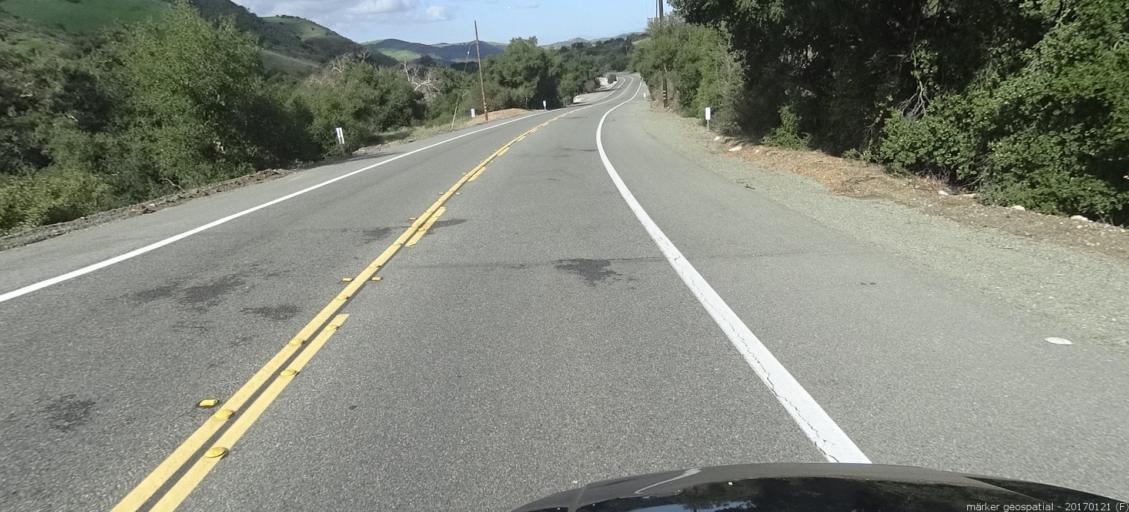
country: US
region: California
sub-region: Orange County
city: Foothill Ranch
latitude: 33.7532
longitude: -117.6936
